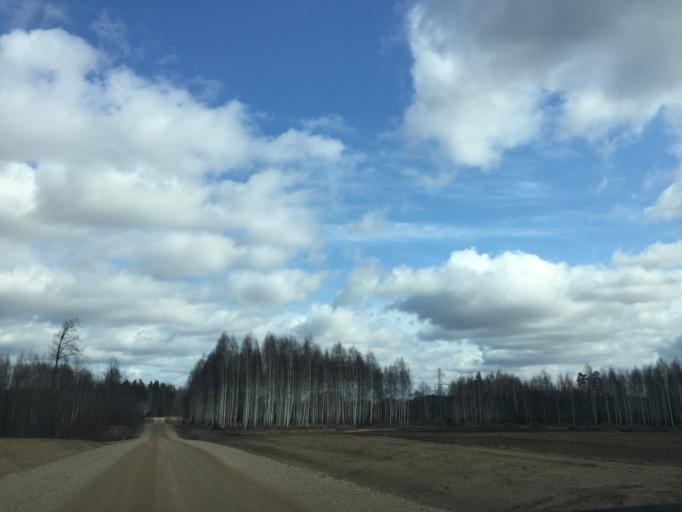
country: LV
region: Vecumnieki
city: Vecumnieki
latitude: 56.5947
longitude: 24.6124
